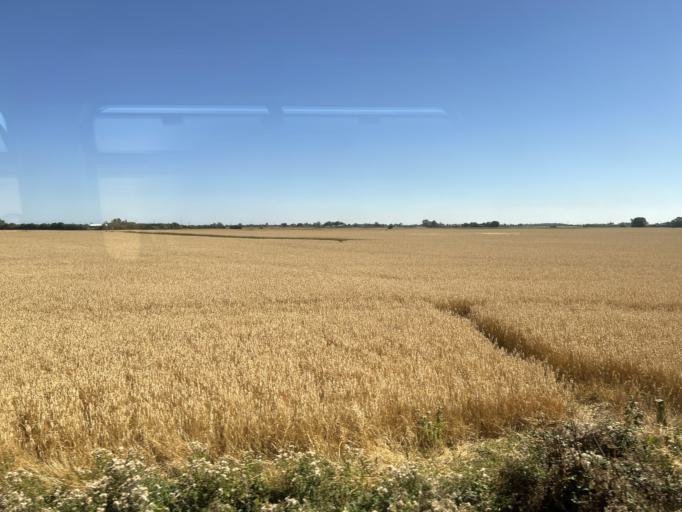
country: GB
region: England
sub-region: Lincolnshire
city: Spilsby
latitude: 53.1304
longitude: 0.1495
